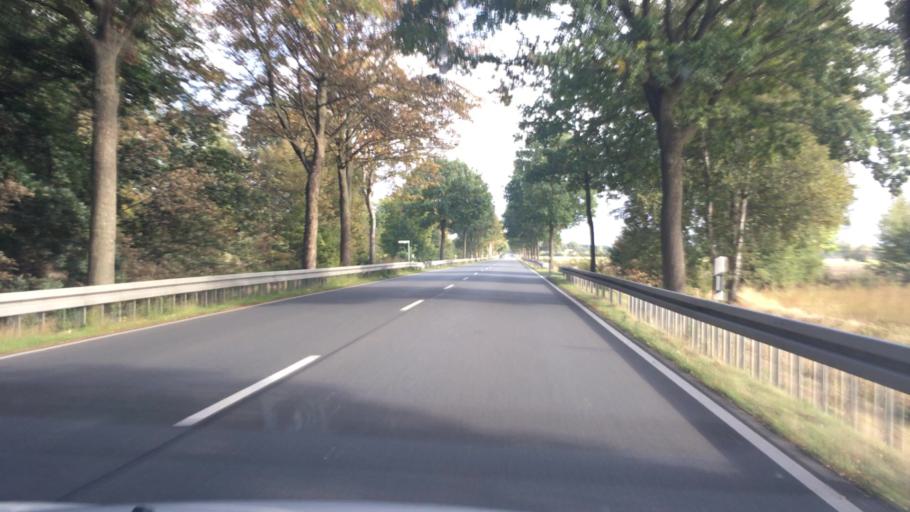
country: DE
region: Lower Saxony
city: Barver
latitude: 52.6104
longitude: 8.5516
